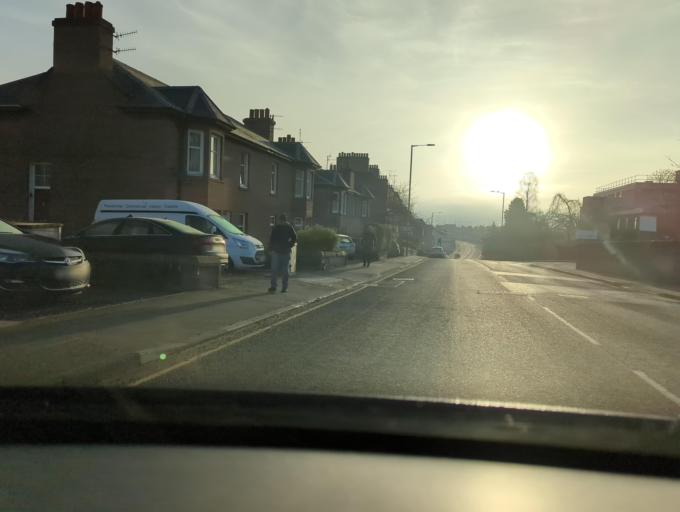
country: GB
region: Scotland
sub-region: Perth and Kinross
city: Perth
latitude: 56.3985
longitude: -3.4563
